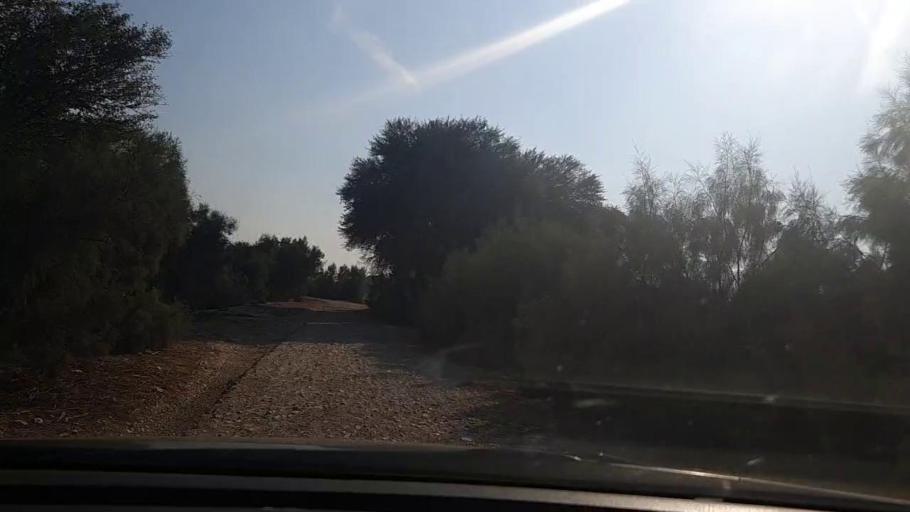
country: PK
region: Sindh
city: Sehwan
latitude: 26.3096
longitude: 68.0010
